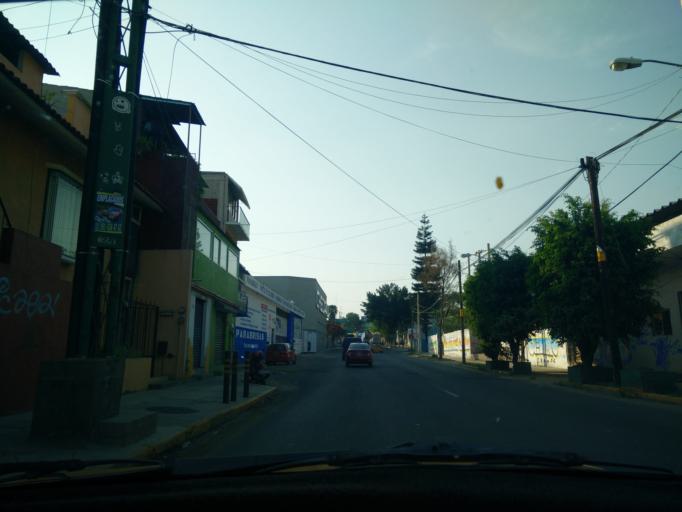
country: MX
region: Oaxaca
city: Oaxaca de Juarez
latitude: 17.0782
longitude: -96.7408
